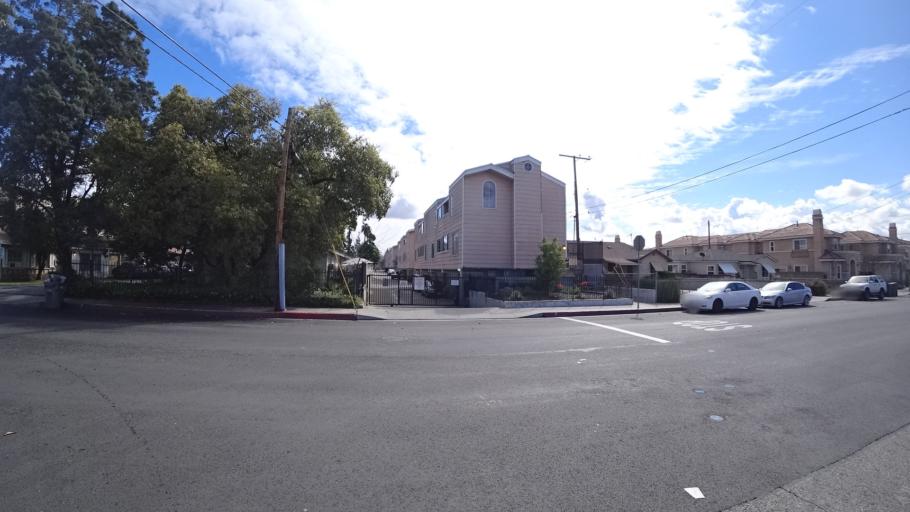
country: US
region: California
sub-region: Los Angeles County
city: Baldwin Park
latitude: 34.0885
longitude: -117.9671
